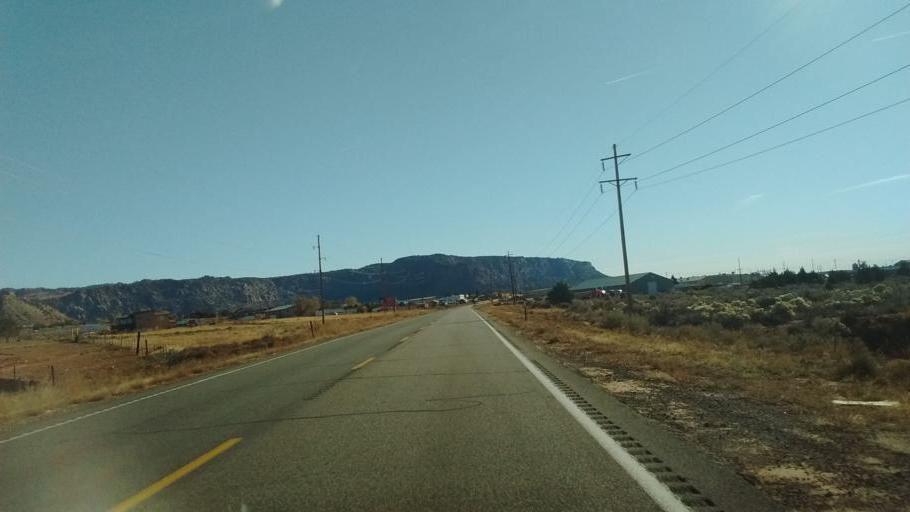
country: US
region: Arizona
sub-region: Mohave County
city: Colorado City
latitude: 37.0073
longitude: -113.0091
